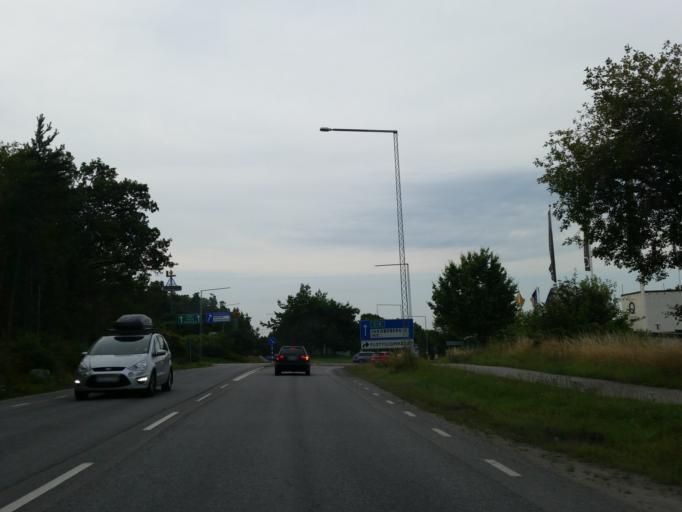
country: SE
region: Stockholm
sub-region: Jarfalla Kommun
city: Jakobsberg
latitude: 59.4169
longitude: 17.8547
